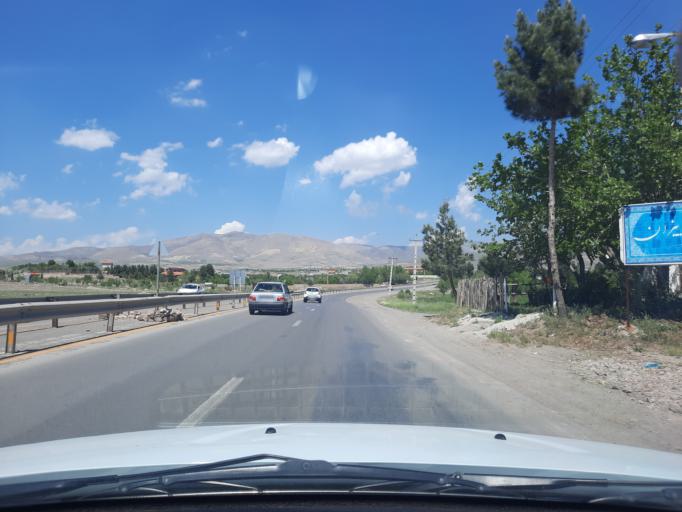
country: IR
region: Qazvin
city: Alvand
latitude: 36.2923
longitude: 50.1350
